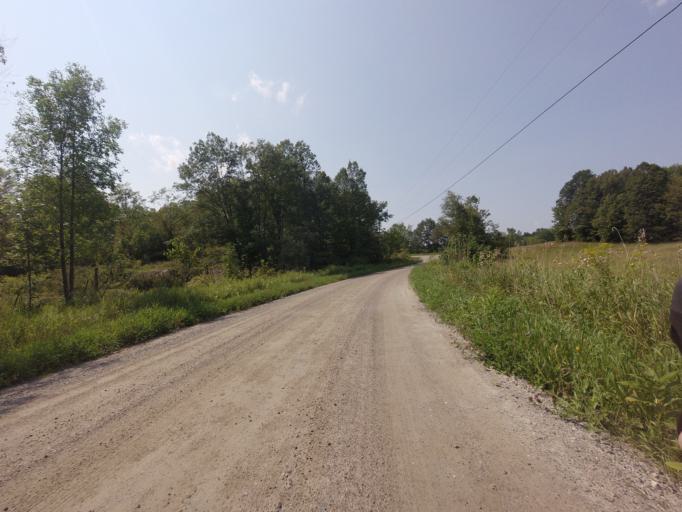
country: CA
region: Ontario
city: Kingston
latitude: 44.6403
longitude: -76.6727
